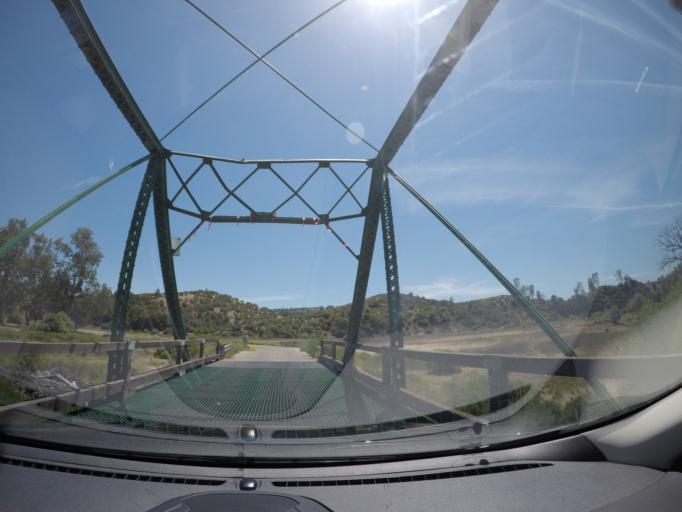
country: US
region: California
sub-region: Monterey County
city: King City
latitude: 35.9844
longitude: -121.2393
